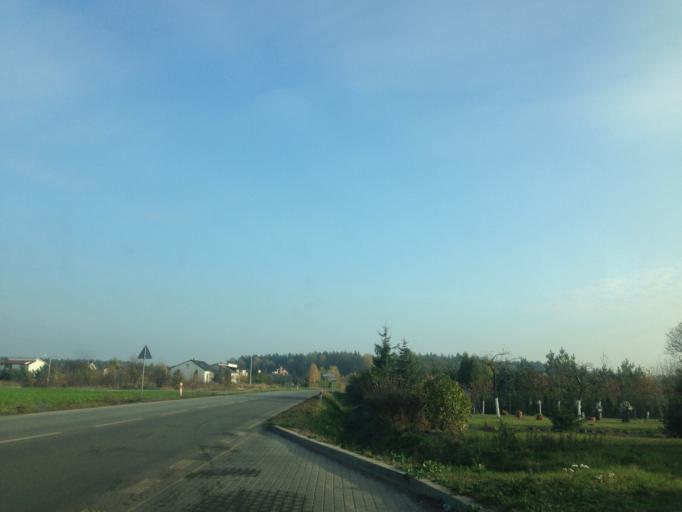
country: PL
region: Kujawsko-Pomorskie
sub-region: Powiat wabrzeski
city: Wabrzezno
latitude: 53.2638
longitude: 18.9971
